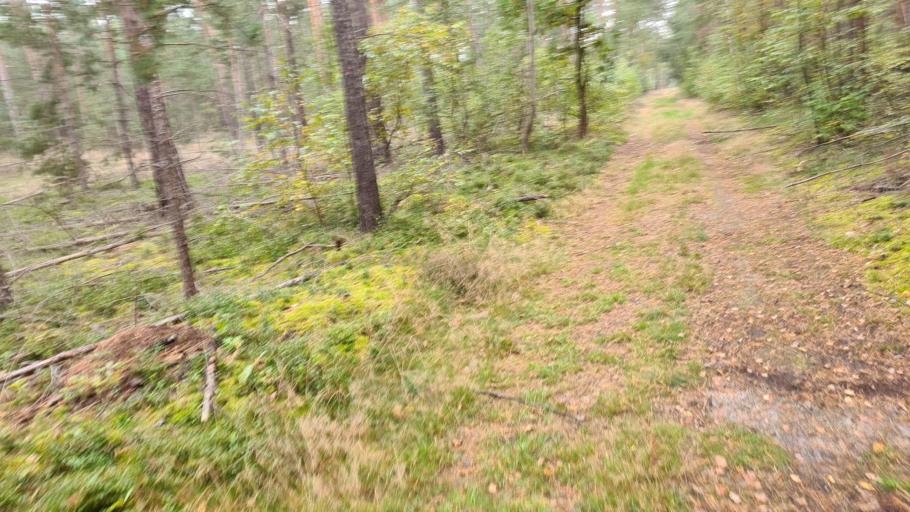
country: DE
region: Brandenburg
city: Schonewalde
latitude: 51.6320
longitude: 13.6115
